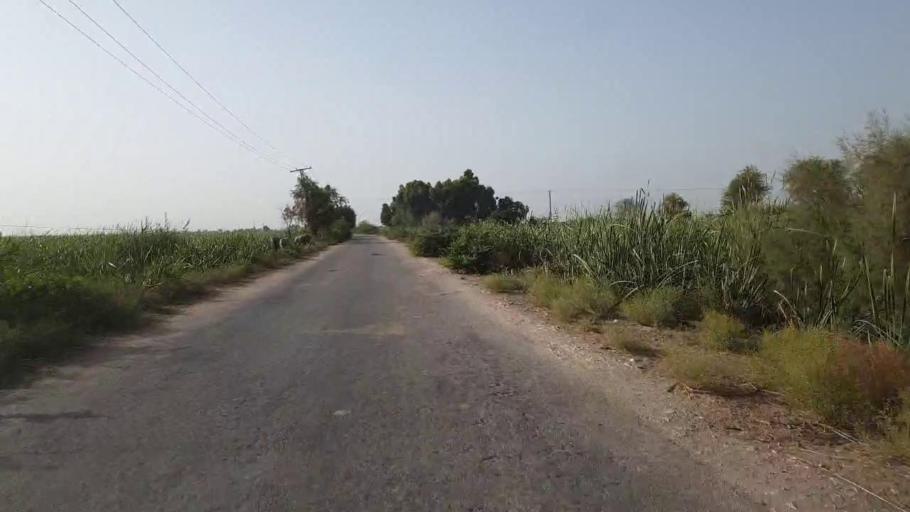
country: PK
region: Sindh
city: Jam Sahib
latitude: 26.4050
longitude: 68.8773
